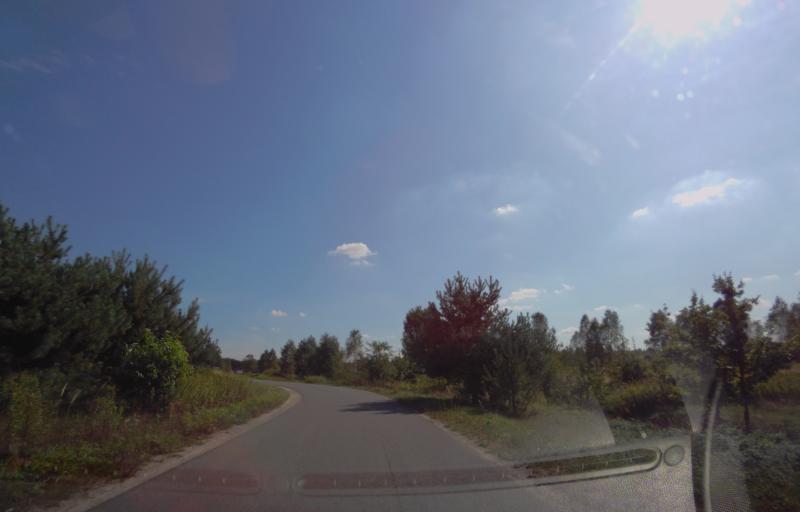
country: PL
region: Subcarpathian Voivodeship
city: Nowa Sarzyna
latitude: 50.2916
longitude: 22.3068
